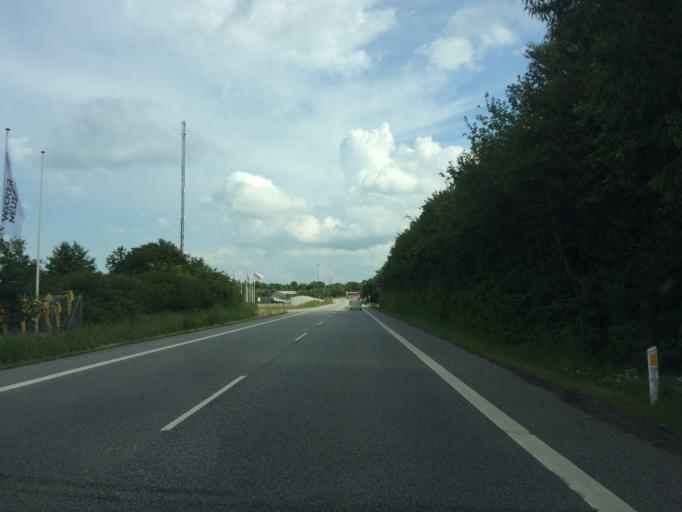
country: DK
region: South Denmark
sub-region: Fredericia Kommune
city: Snoghoj
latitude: 55.5277
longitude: 9.7100
